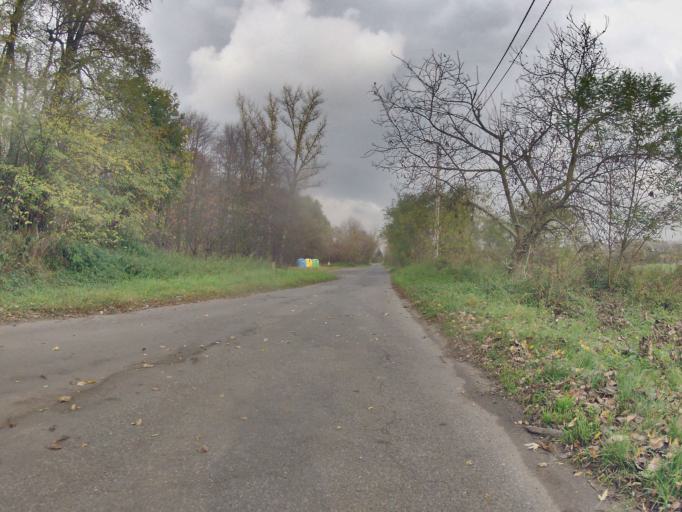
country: PL
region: Lesser Poland Voivodeship
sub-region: Powiat wielicki
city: Wegrzce Wielkie
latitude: 50.0474
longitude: 20.0999
